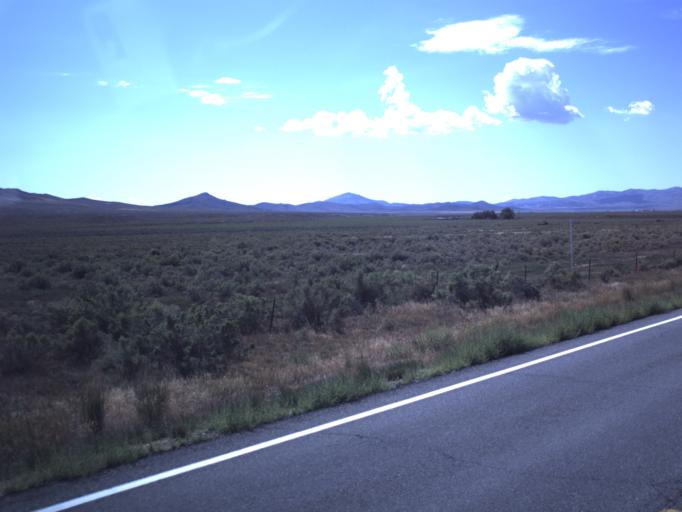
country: US
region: Utah
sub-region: Tooele County
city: Tooele
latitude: 40.1696
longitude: -112.4293
